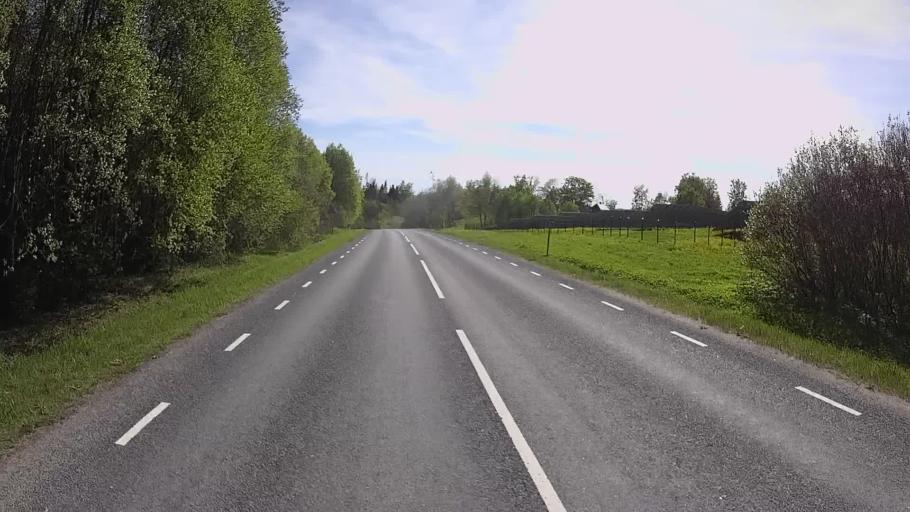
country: EE
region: Vorumaa
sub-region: Antsla vald
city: Vana-Antsla
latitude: 57.9801
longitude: 26.4676
